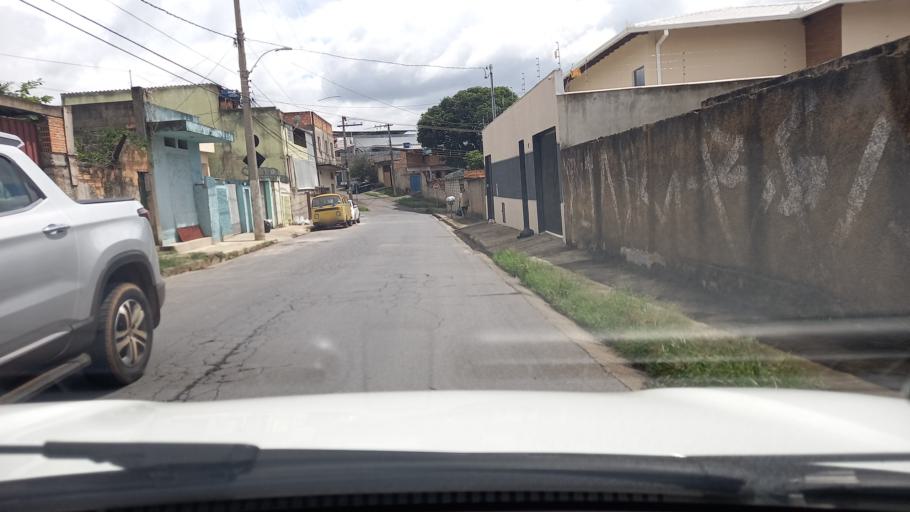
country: BR
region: Minas Gerais
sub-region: Contagem
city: Contagem
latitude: -19.9005
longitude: -44.0195
